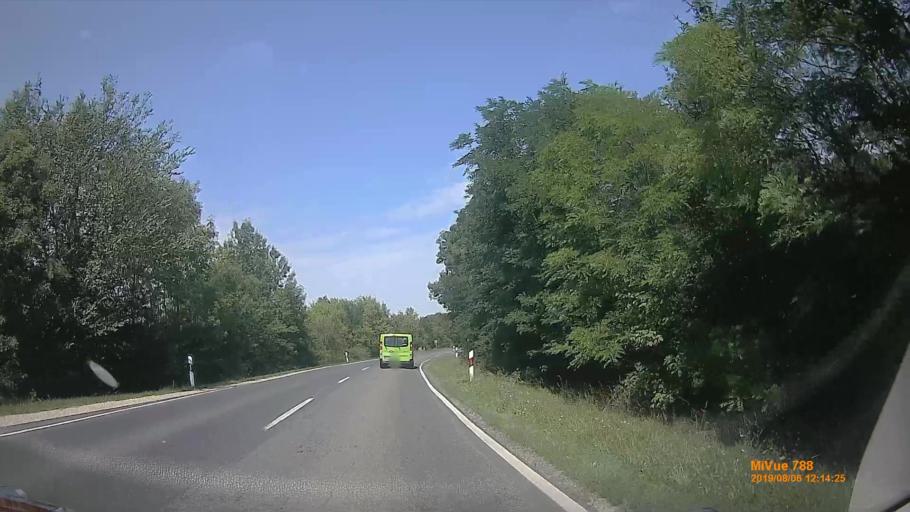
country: HU
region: Vas
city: Vasvar
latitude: 47.1391
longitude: 16.8297
